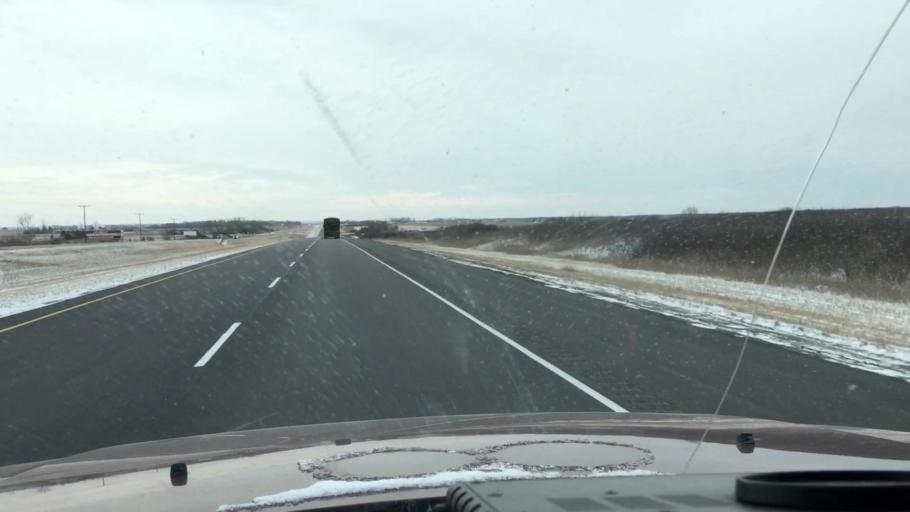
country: CA
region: Saskatchewan
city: Saskatoon
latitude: 51.9274
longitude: -106.5341
